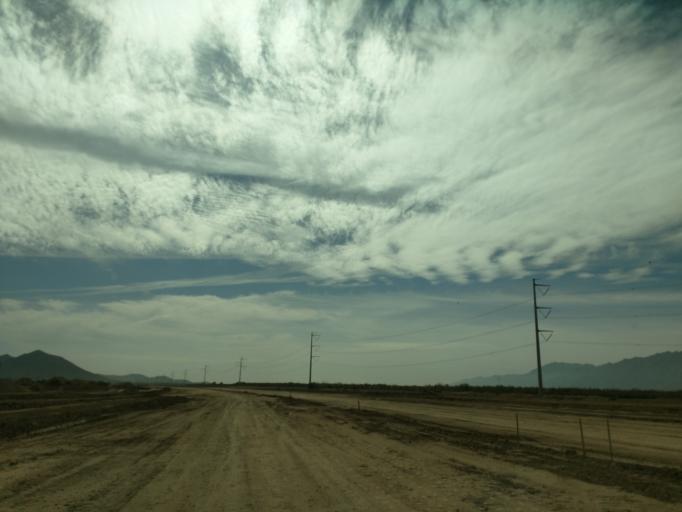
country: US
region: Arizona
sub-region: Maricopa County
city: Laveen
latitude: 33.3459
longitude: -112.1881
